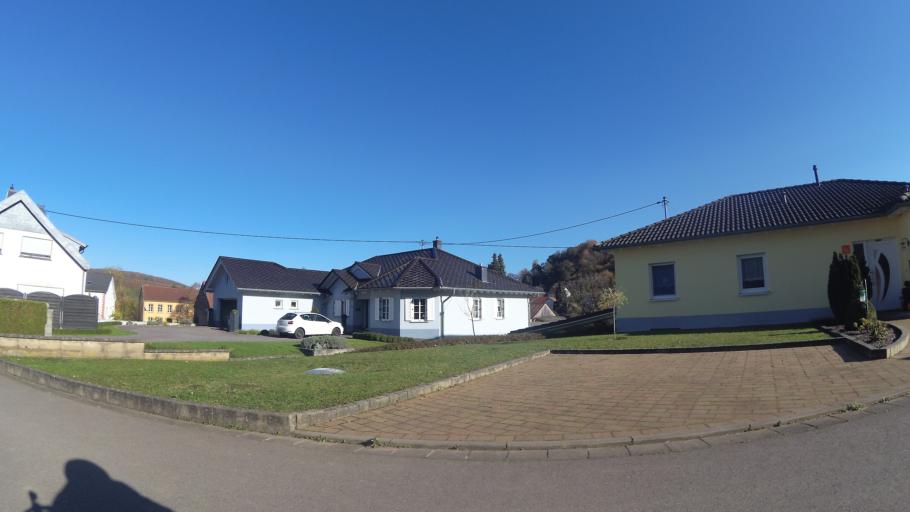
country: DE
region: Saarland
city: Losheim
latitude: 49.4863
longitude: 6.7727
